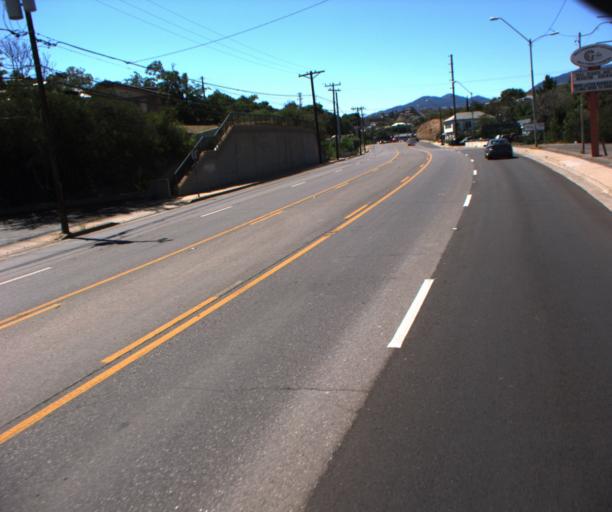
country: US
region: Arizona
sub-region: Gila County
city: Globe
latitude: 33.4063
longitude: -110.7932
